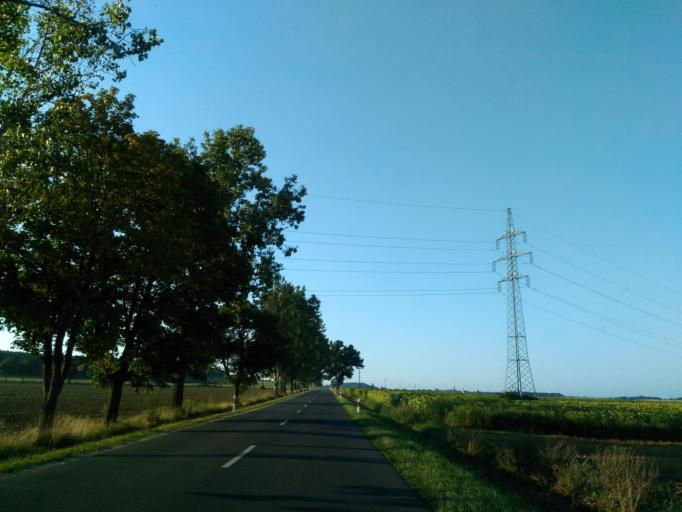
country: HU
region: Veszprem
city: Zanka
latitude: 46.9636
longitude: 17.6995
